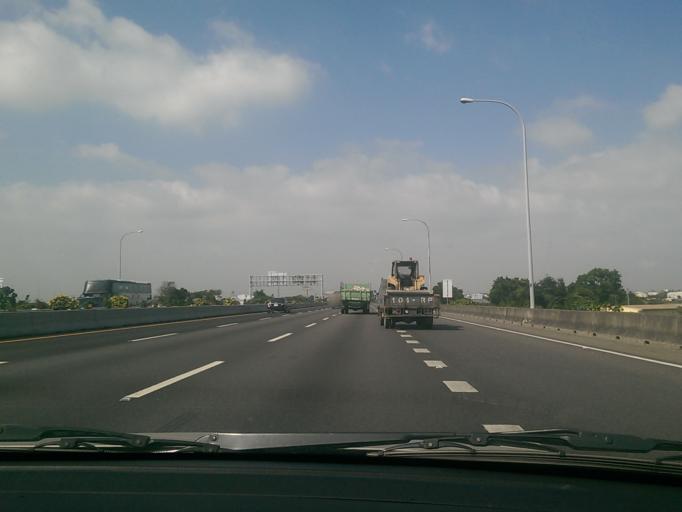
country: TW
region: Taiwan
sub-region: Changhua
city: Chang-hua
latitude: 23.9596
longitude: 120.5066
